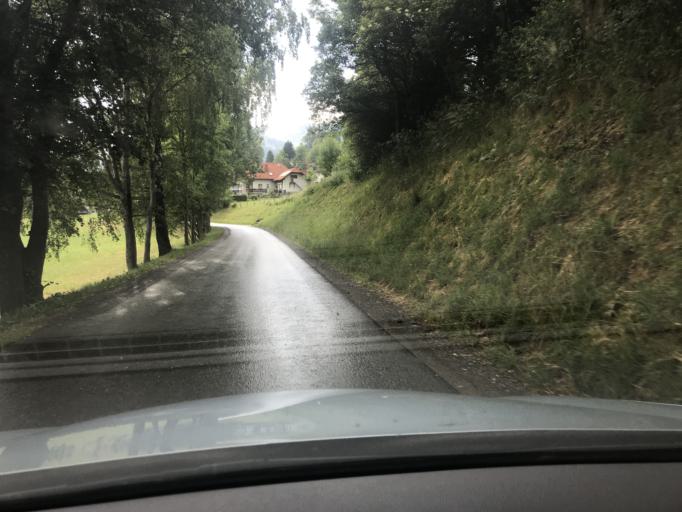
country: AT
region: Styria
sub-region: Politischer Bezirk Murau
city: Sankt Peter am Kammersberg
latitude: 47.1893
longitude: 14.1778
